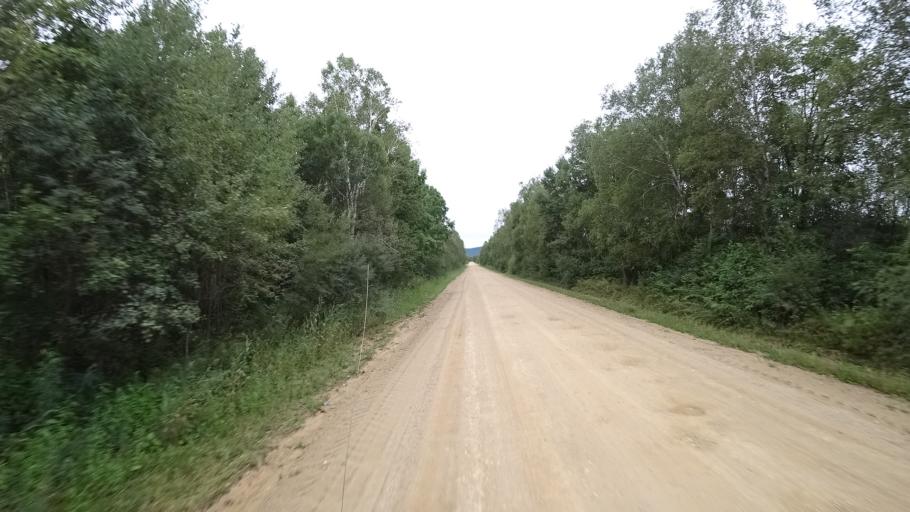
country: RU
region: Primorskiy
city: Rettikhovka
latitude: 44.1594
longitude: 132.7002
